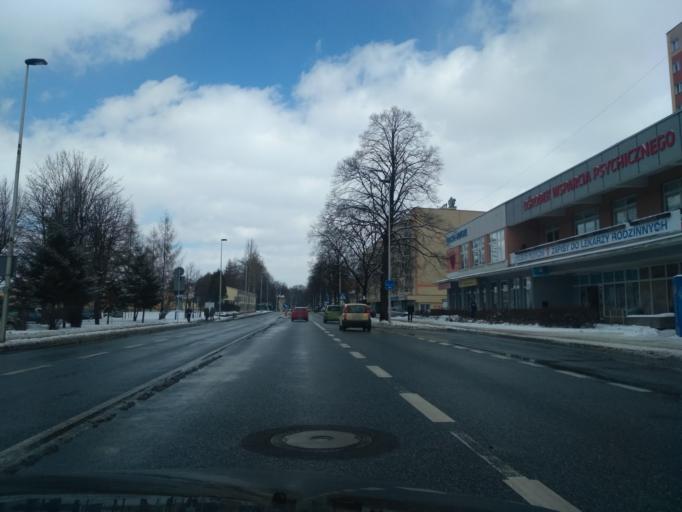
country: PL
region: Subcarpathian Voivodeship
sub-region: Rzeszow
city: Rzeszow
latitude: 50.0264
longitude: 21.9907
